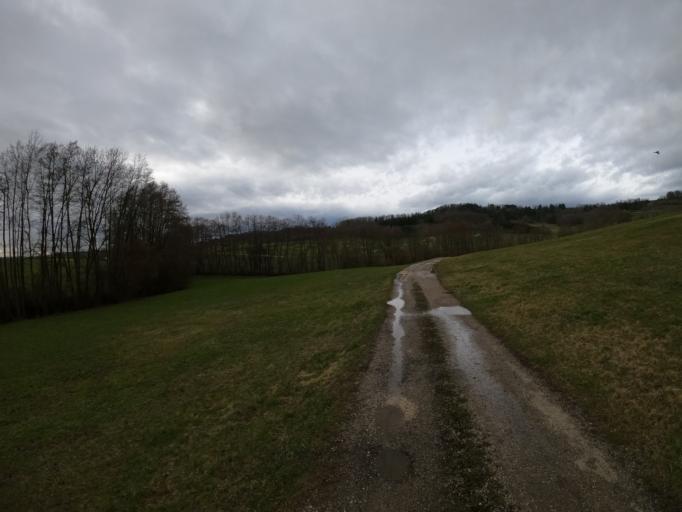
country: DE
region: Baden-Wuerttemberg
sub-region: Regierungsbezirk Stuttgart
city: Waschenbeuren
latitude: 48.7314
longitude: 9.6923
